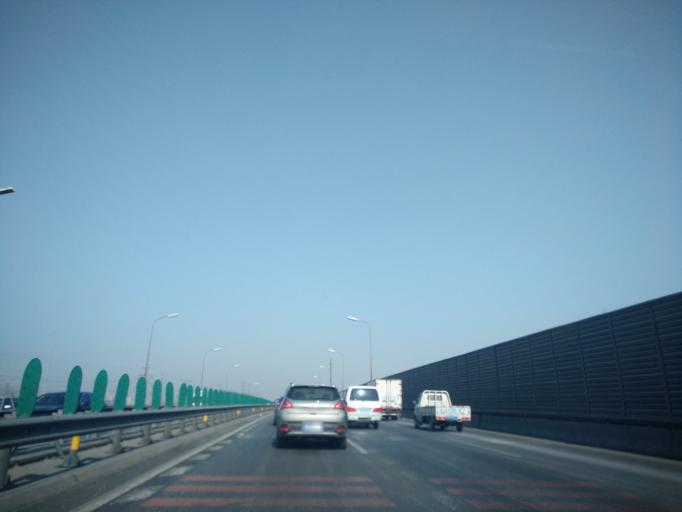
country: CN
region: Beijing
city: Wangjing
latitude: 39.9772
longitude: 116.5120
